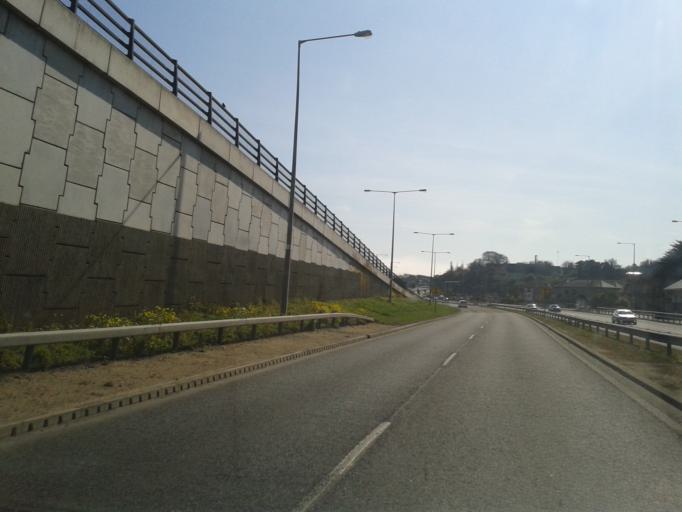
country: IE
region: Leinster
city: Loughlinstown
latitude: 53.2468
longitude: -6.1365
